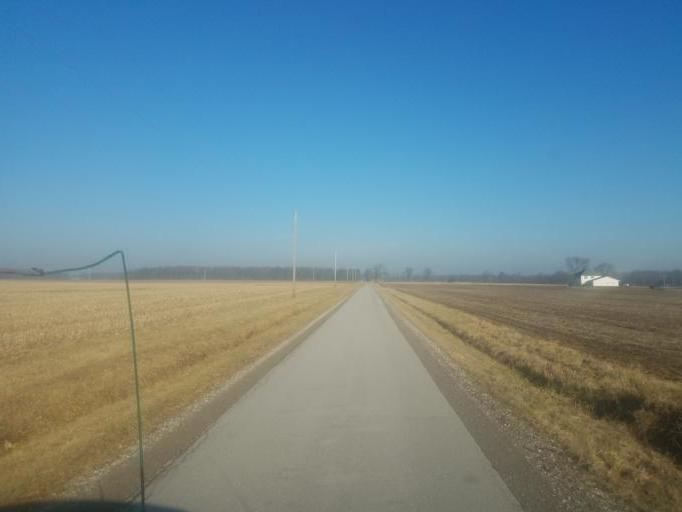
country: US
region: Ohio
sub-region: Huron County
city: Willard
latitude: 41.0340
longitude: -82.9390
